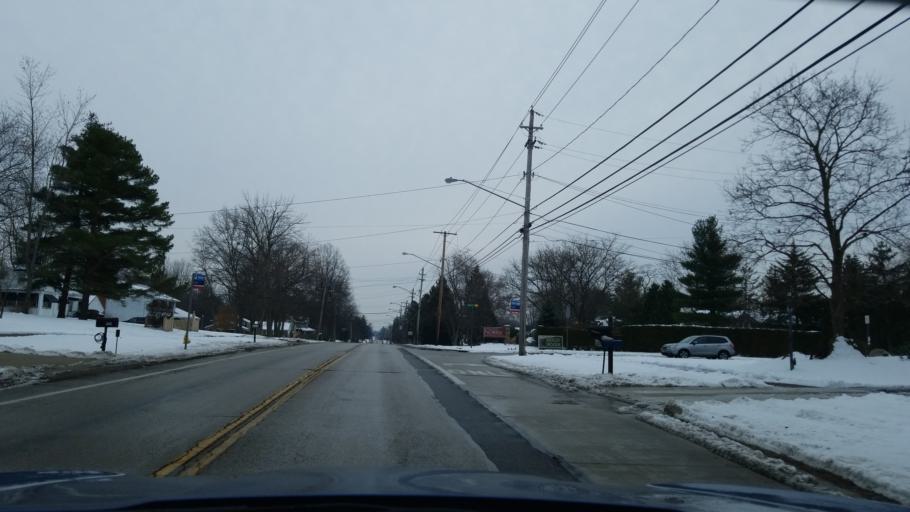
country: US
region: Ohio
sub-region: Cuyahoga County
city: North Royalton
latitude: 41.3139
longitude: -81.7193
